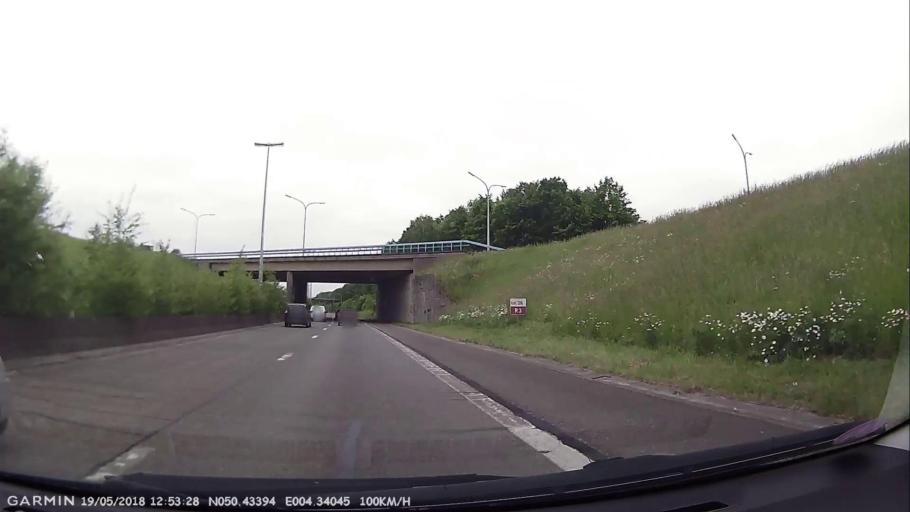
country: BE
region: Wallonia
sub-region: Province du Hainaut
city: Courcelles
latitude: 50.4342
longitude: 4.3402
